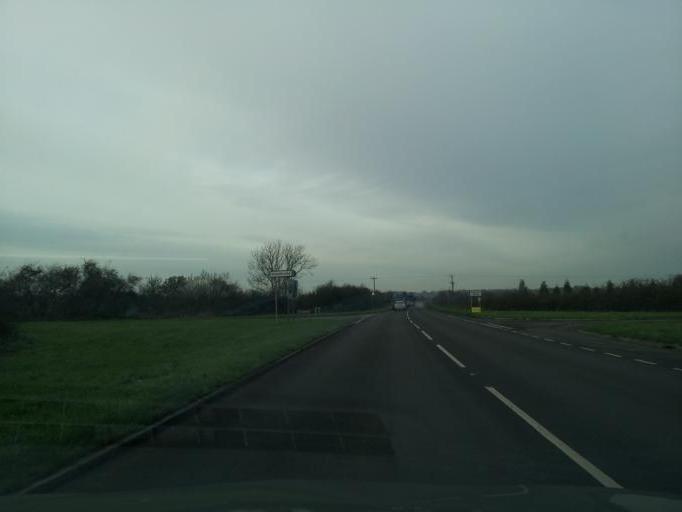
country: GB
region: England
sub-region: Buckinghamshire
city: Aylesbury
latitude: 51.8430
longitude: -0.7737
